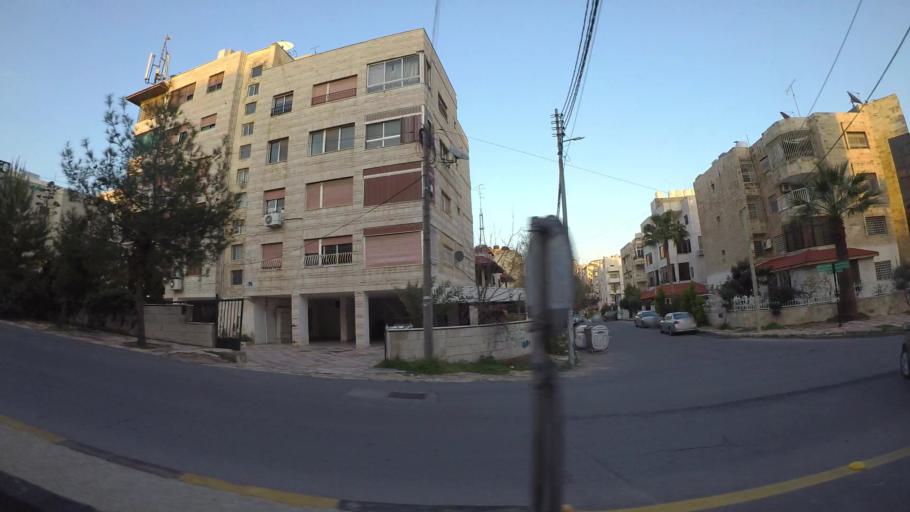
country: JO
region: Amman
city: Al Jubayhah
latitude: 31.9949
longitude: 35.8769
